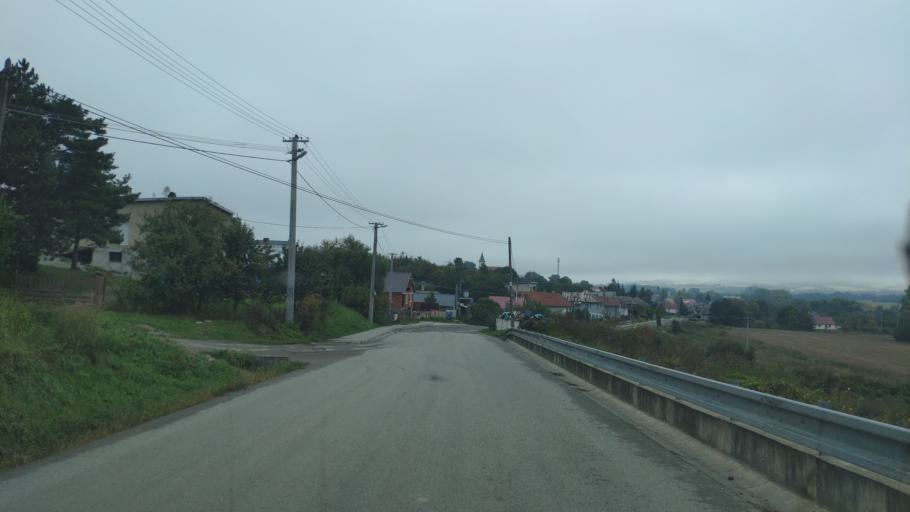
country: SK
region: Kosicky
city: Kosice
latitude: 48.8202
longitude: 21.4097
